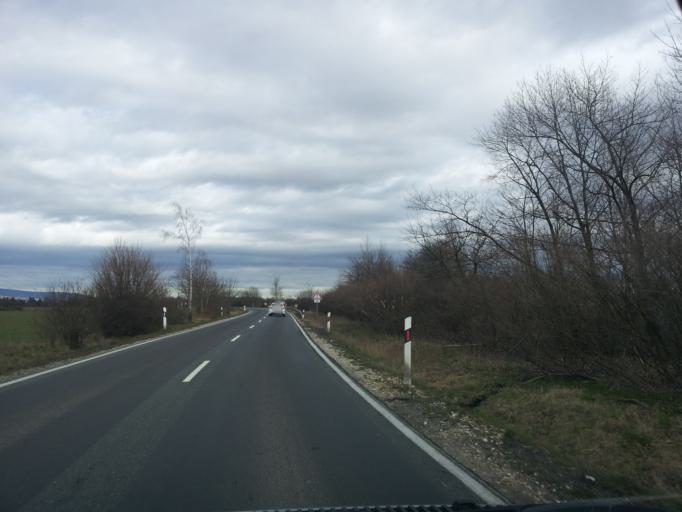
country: HU
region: Vas
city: Gencsapati
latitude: 47.3079
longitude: 16.5954
